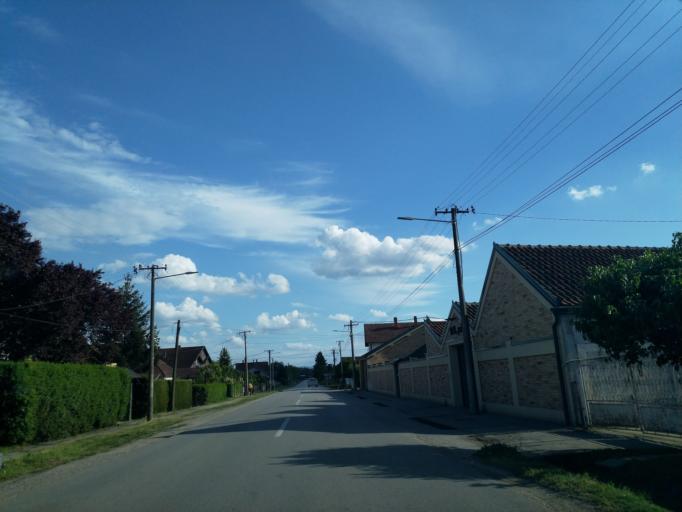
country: RS
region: Central Serbia
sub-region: Sumadijski Okrug
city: Lapovo
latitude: 44.1844
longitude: 21.0917
